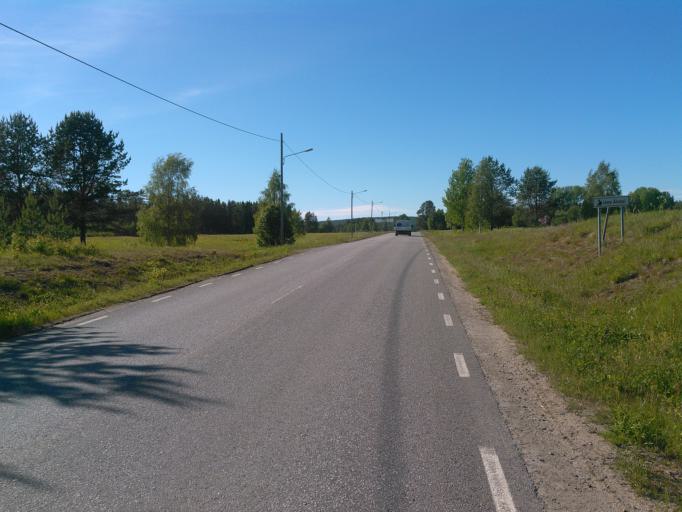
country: SE
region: Vaesterbotten
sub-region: Umea Kommun
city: Roback
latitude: 63.8265
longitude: 20.1206
